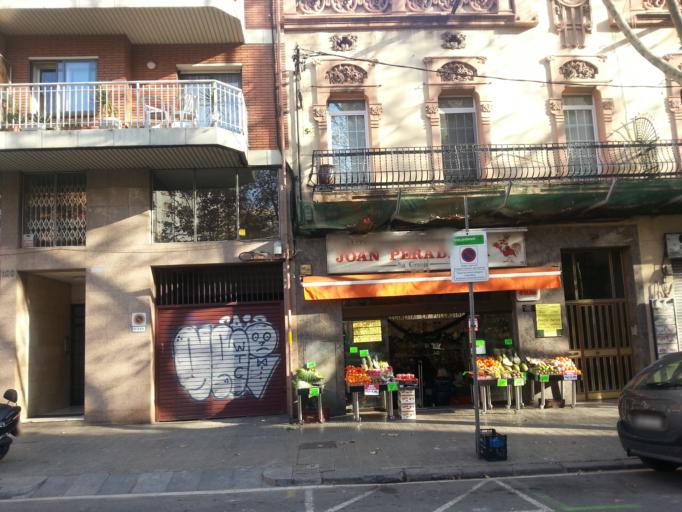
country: ES
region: Catalonia
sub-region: Provincia de Barcelona
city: Ciutat Vella
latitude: 41.3928
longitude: 2.1873
